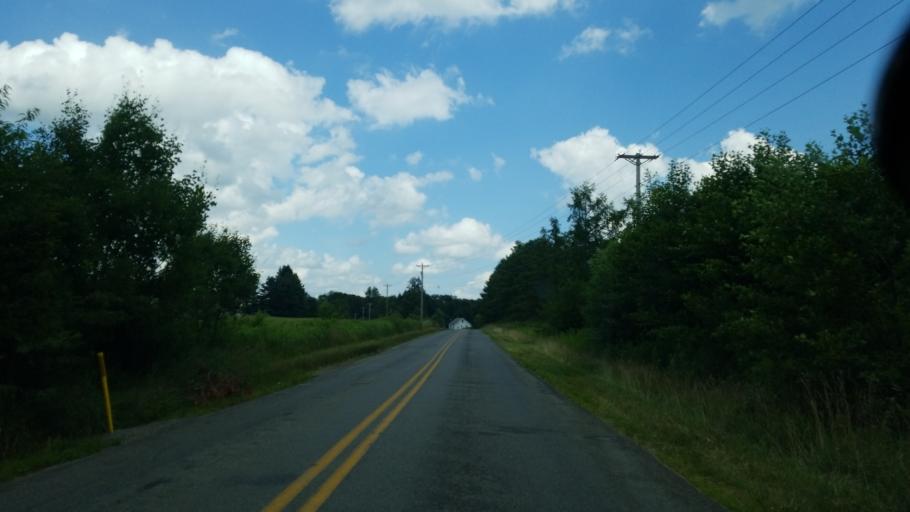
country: US
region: Pennsylvania
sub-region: Jefferson County
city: Brookville
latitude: 41.2393
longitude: -79.0180
